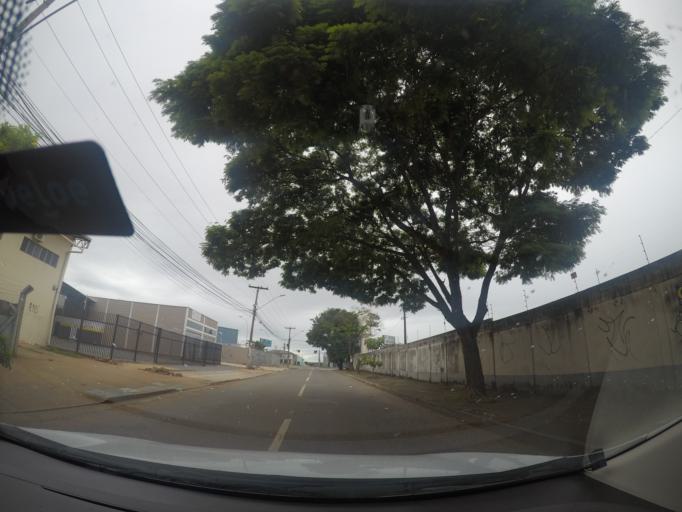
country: BR
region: Goias
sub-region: Goiania
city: Goiania
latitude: -16.6524
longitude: -49.3182
